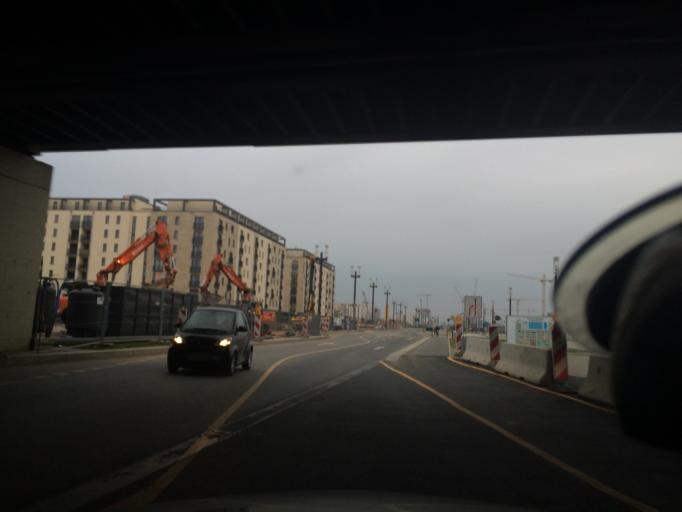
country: DE
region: Hesse
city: Niederrad
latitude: 50.1086
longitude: 8.6436
